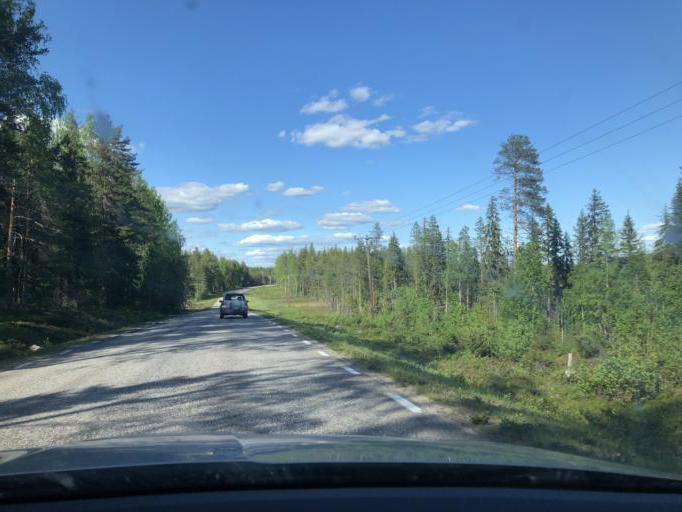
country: SE
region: Norrbotten
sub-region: Kalix Kommun
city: Kalix
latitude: 66.0426
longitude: 23.1773
